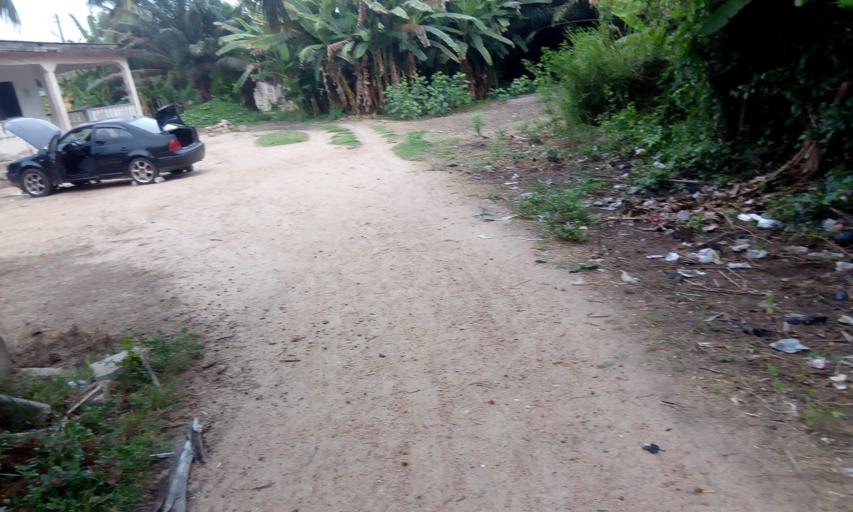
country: GH
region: Central
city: Winneba
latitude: 5.3538
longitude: -0.6250
